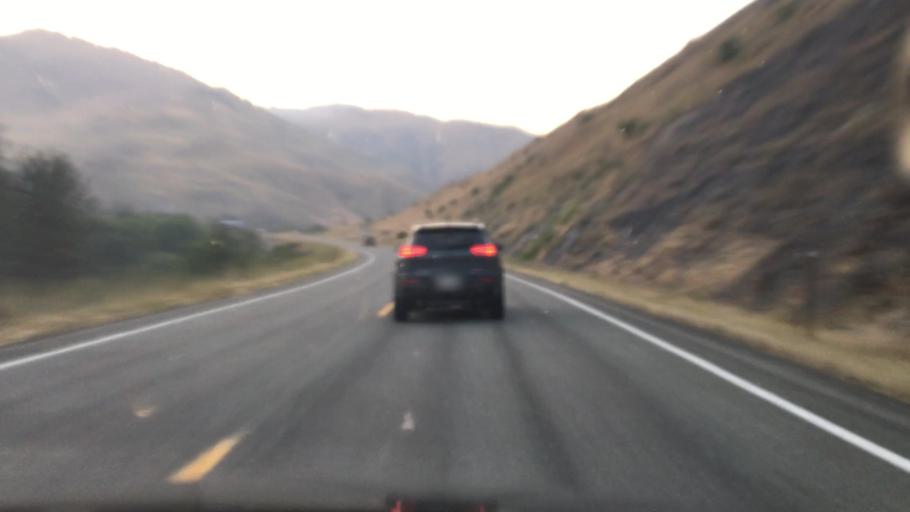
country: US
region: Idaho
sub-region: Idaho County
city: Grangeville
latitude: 45.5307
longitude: -116.3040
